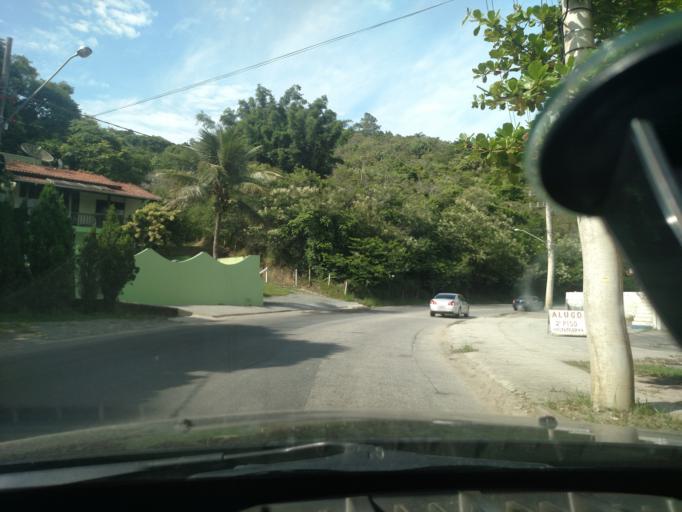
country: BR
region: Santa Catarina
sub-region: Porto Belo
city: Porto Belo
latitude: -27.1469
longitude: -48.5326
